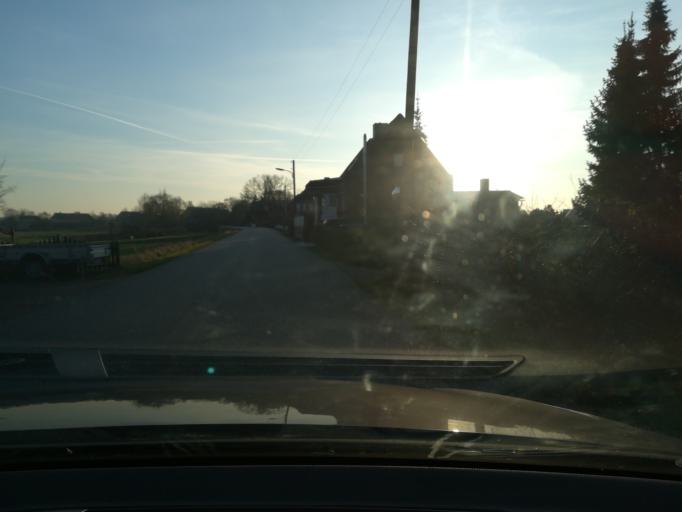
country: DE
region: Hamburg
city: Bergedorf
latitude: 53.4335
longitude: 10.1988
